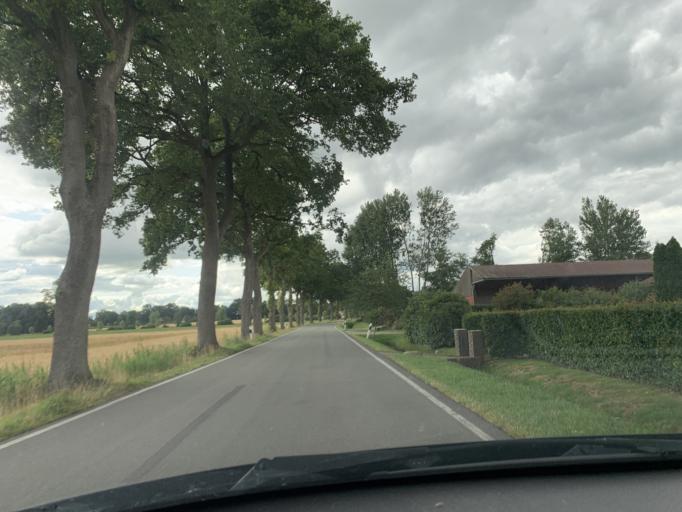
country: DE
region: Lower Saxony
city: Westerstede
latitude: 53.2222
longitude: 7.9053
